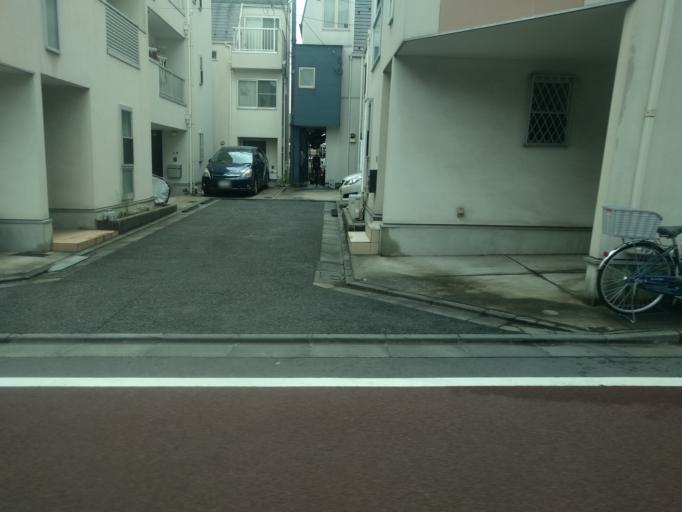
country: JP
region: Tokyo
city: Tokyo
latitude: 35.6056
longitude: 139.6776
